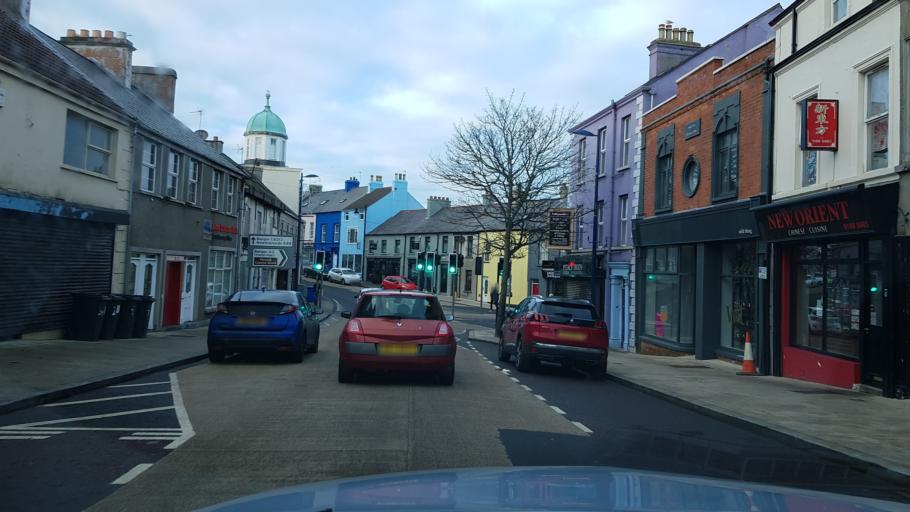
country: GB
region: Northern Ireland
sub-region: Down District
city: Donaghadee
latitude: 54.6422
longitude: -5.5371
